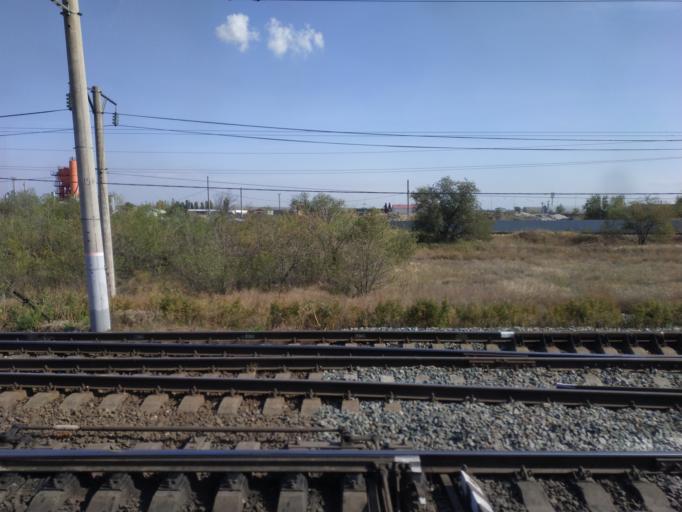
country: RU
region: Volgograd
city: Gumrak
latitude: 48.7913
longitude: 44.3669
